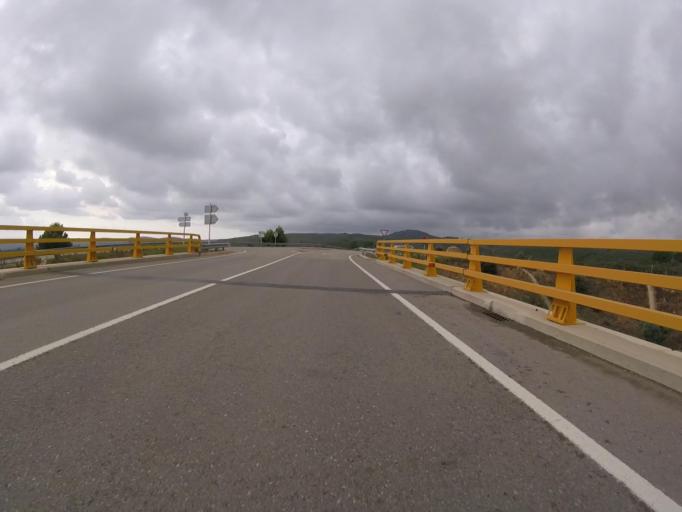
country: ES
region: Valencia
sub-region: Provincia de Castello
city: Benlloch
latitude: 40.2156
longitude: 0.0953
